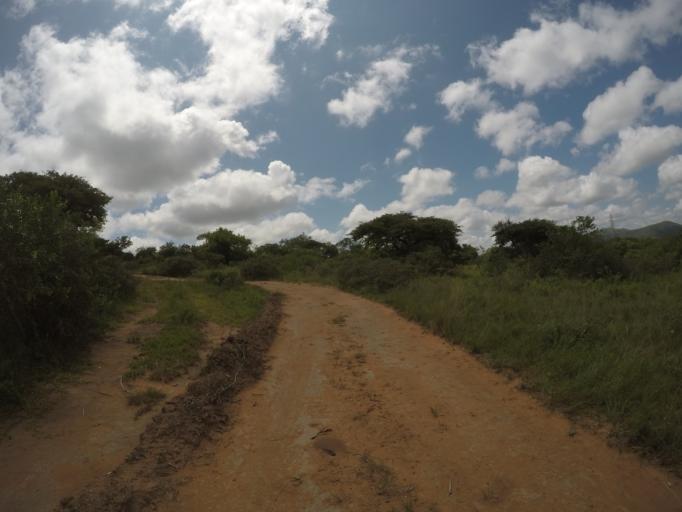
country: ZA
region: KwaZulu-Natal
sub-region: uThungulu District Municipality
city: Empangeni
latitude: -28.5865
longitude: 31.8341
